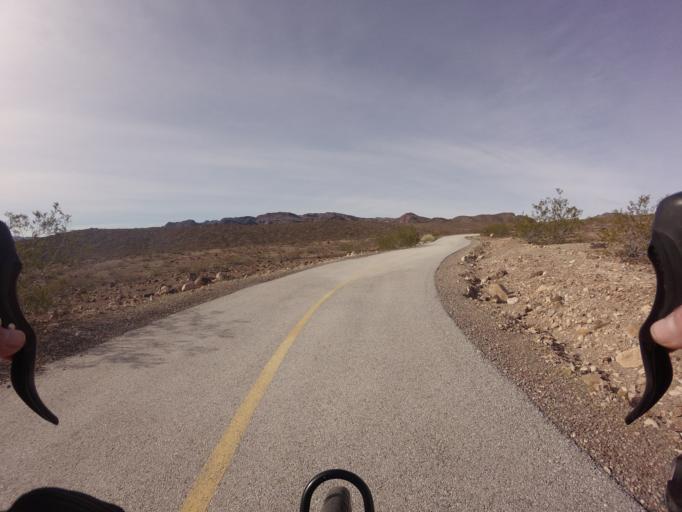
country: US
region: Nevada
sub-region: Clark County
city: Boulder City
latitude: 36.0767
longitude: -114.8173
